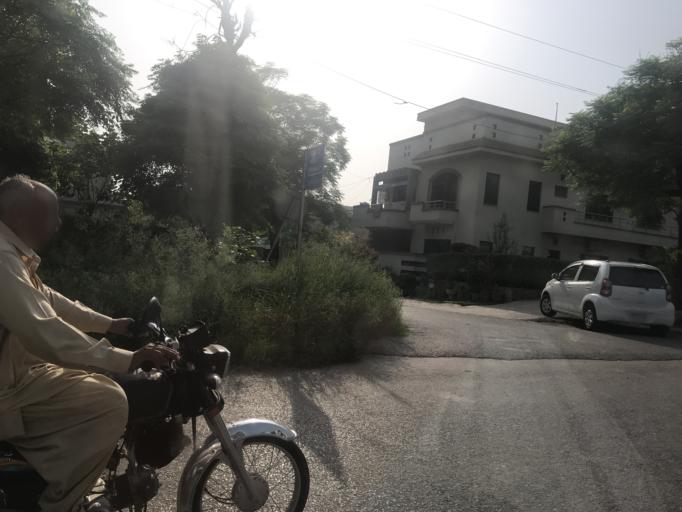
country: PK
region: Islamabad
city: Islamabad
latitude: 33.6977
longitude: 73.0478
